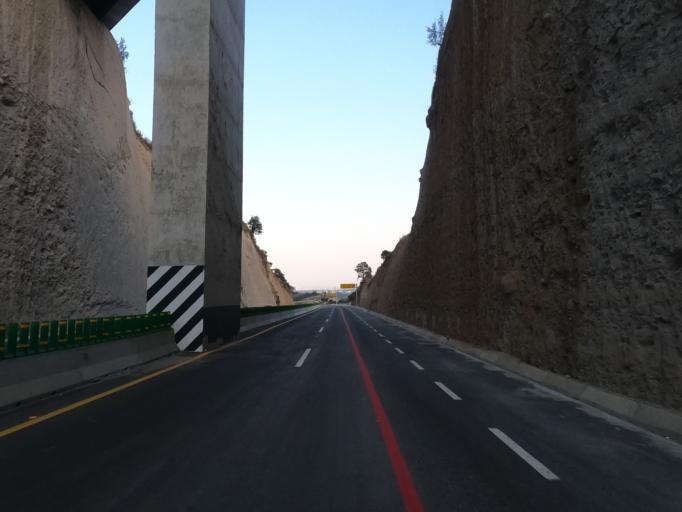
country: MX
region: Mexico
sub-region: Naucalpan de Juarez
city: Llano de las Flores (Barrio del Hueso)
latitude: 19.4229
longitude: -99.3272
